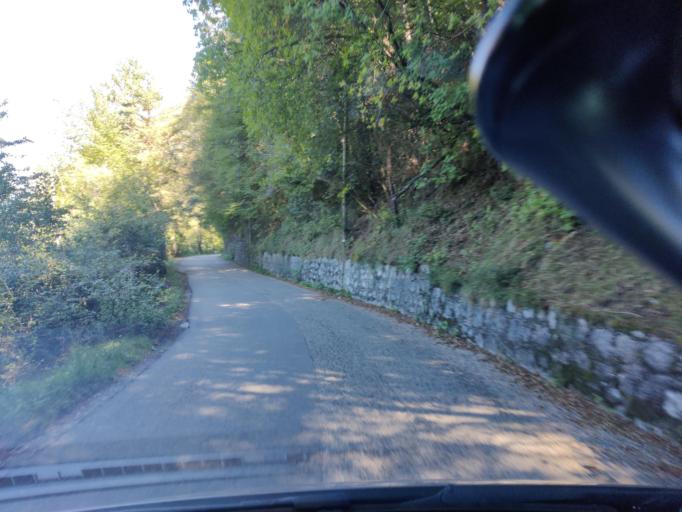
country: IT
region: Lombardy
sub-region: Provincia di Brescia
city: Anfo
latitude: 45.7717
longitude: 10.5214
